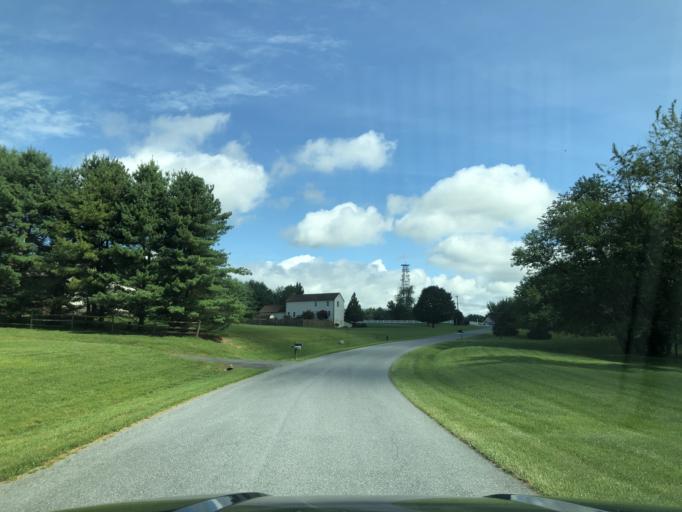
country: US
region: Maryland
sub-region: Howard County
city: Highland
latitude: 39.2131
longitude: -76.9740
